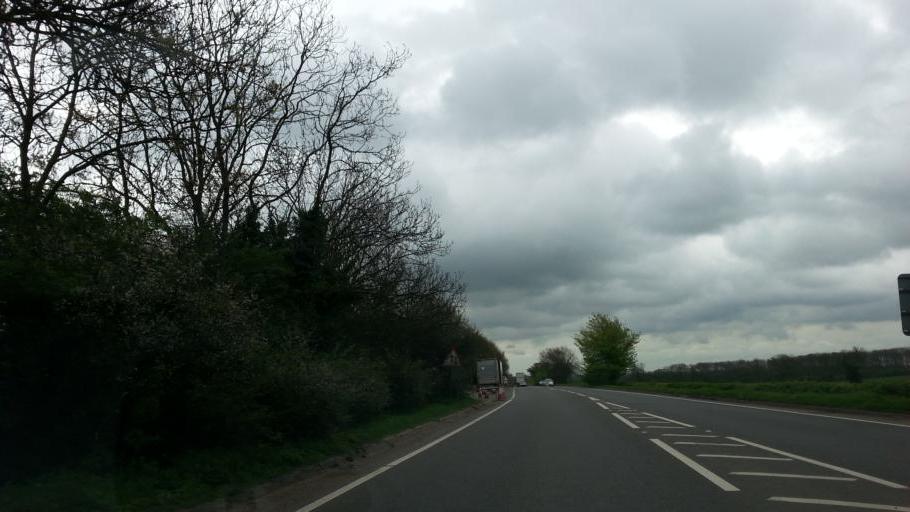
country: GB
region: England
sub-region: Leicestershire
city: Lutterworth
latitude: 52.4216
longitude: -1.2243
